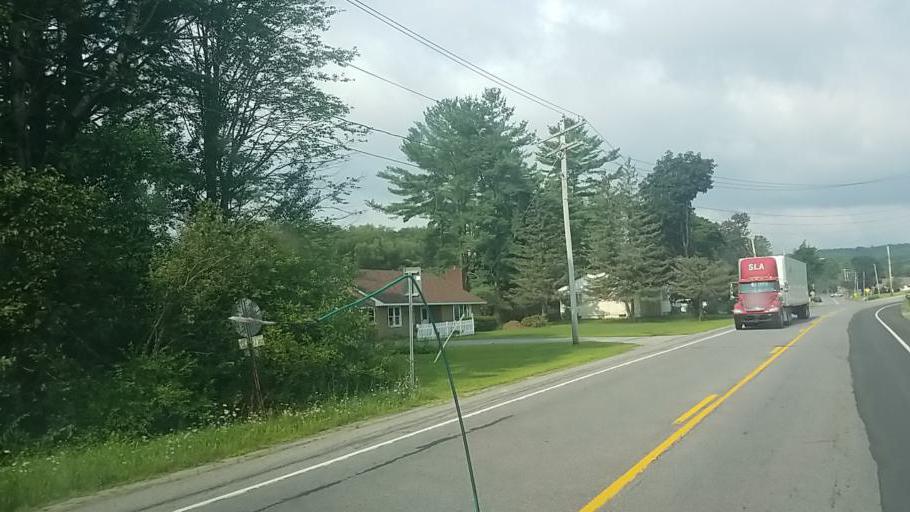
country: US
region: New York
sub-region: Fulton County
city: Gloversville
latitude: 43.0546
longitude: -74.3778
